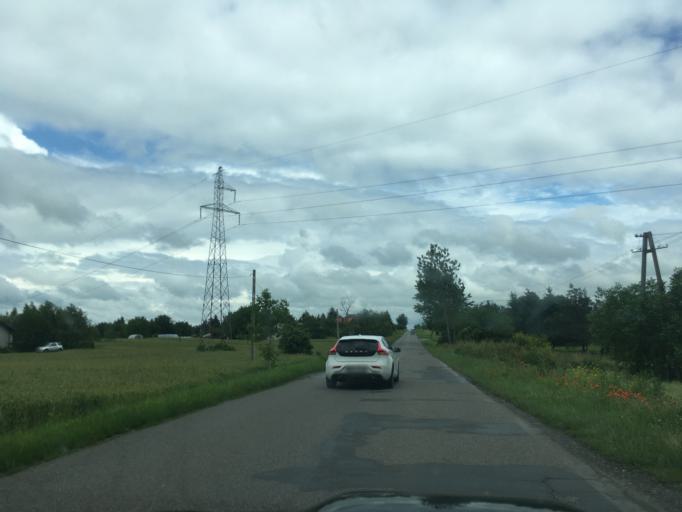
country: PL
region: Lublin Voivodeship
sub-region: Powiat swidnicki
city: Swidnik
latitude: 51.1954
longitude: 22.7151
